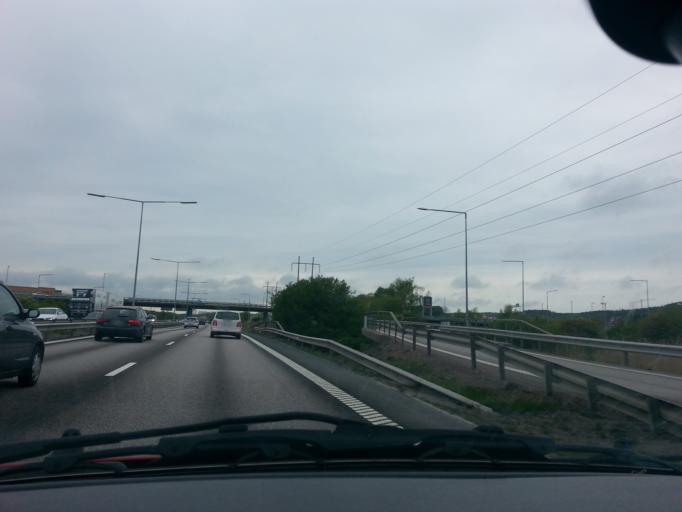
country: SE
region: Vaestra Goetaland
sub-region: Molndal
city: Moelndal
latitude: 57.6445
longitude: 11.9887
